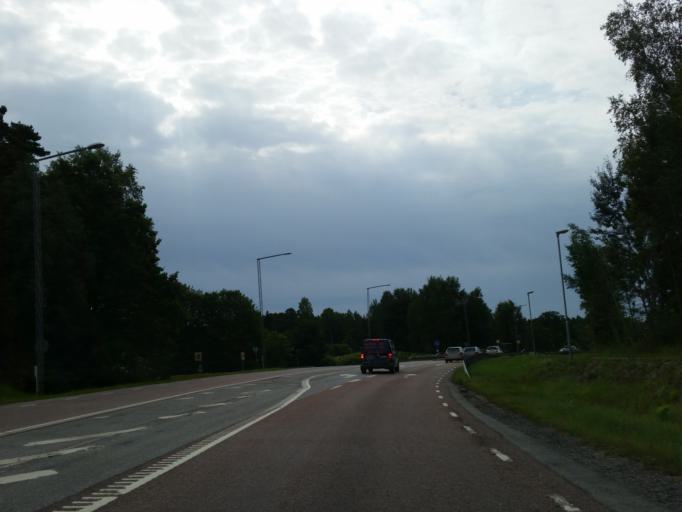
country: SE
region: Stockholm
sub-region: Botkyrka Kommun
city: Alby
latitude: 59.2338
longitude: 17.8425
